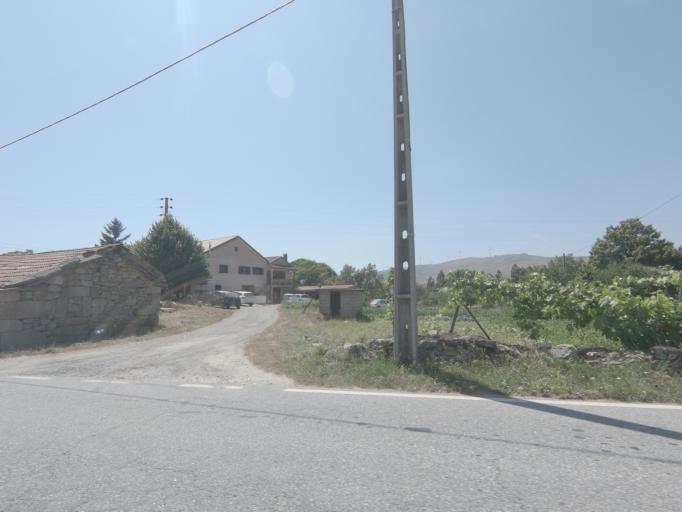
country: PT
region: Viseu
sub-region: Castro Daire
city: Castro Daire
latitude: 40.9634
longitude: -7.8850
